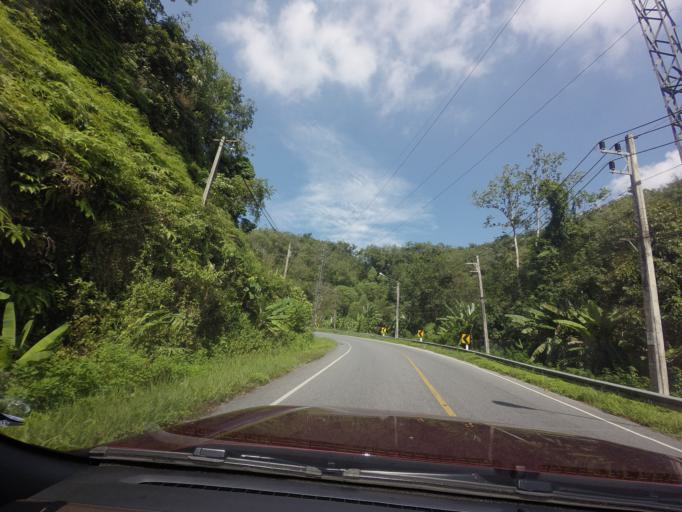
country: TH
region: Yala
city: Betong
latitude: 5.8757
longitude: 101.1336
